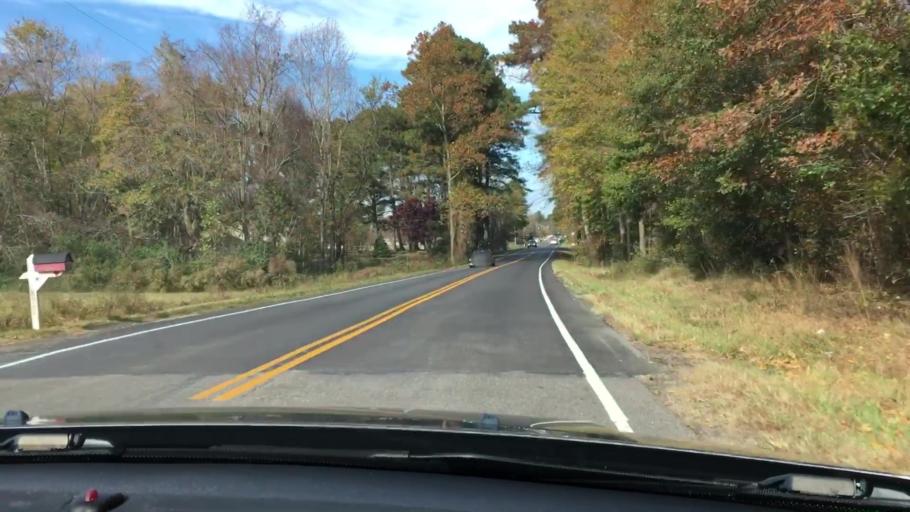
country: US
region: Virginia
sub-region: King William County
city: West Point
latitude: 37.4492
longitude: -76.8399
